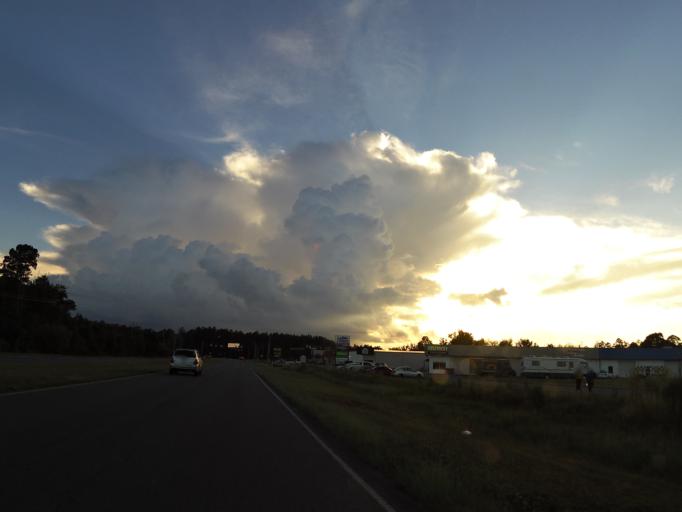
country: US
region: Georgia
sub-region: Camden County
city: St Marys
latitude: 30.7807
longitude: -81.6205
